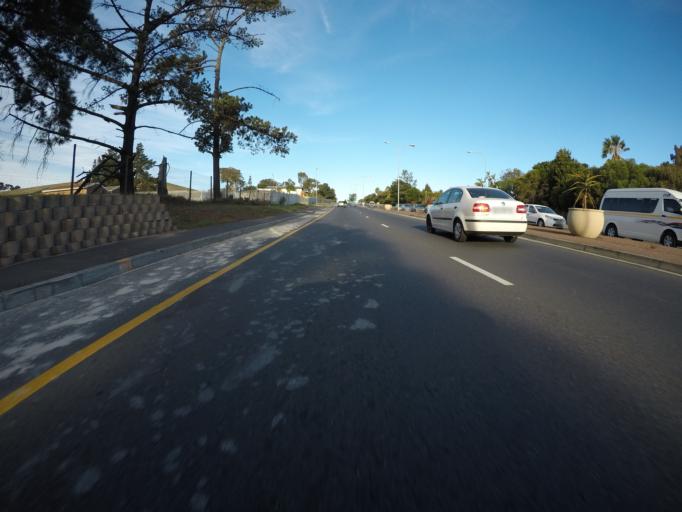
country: ZA
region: Western Cape
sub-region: City of Cape Town
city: Kraaifontein
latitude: -33.8579
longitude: 18.6734
